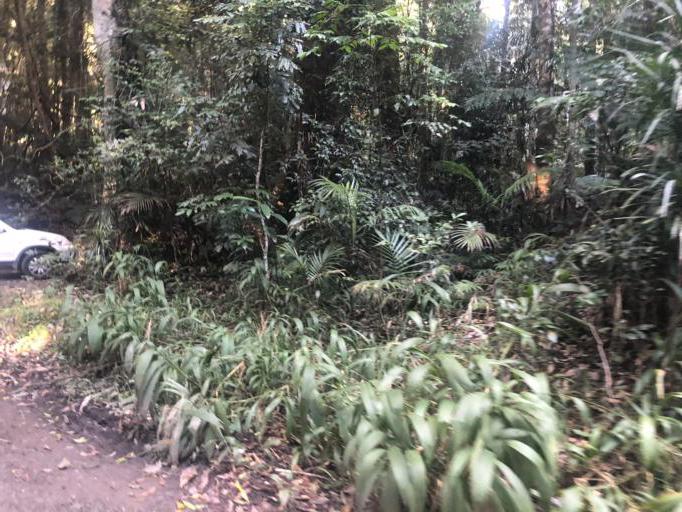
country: AU
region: New South Wales
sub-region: Coffs Harbour
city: Coffs Harbour
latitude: -30.2412
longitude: 153.0952
